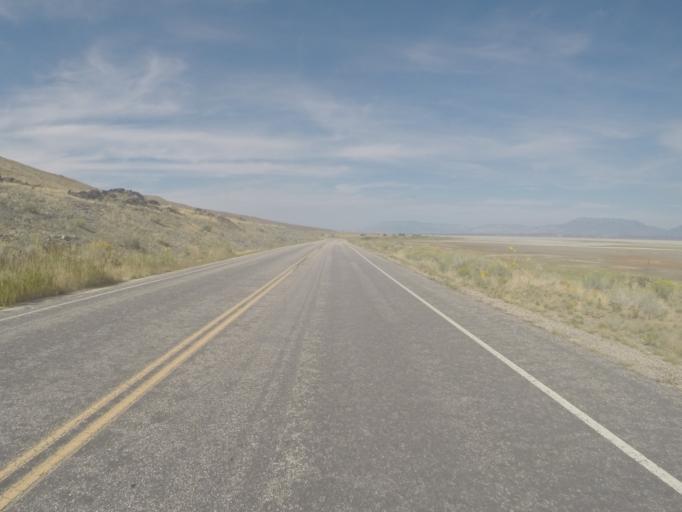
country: US
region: Utah
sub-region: Davis County
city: Syracuse
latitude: 41.0007
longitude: -112.1982
